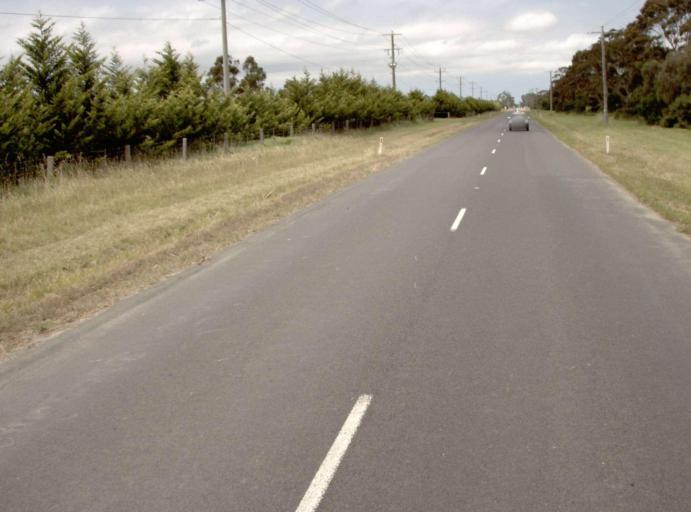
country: AU
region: Victoria
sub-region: Latrobe
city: Traralgon
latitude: -38.5541
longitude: 146.6609
